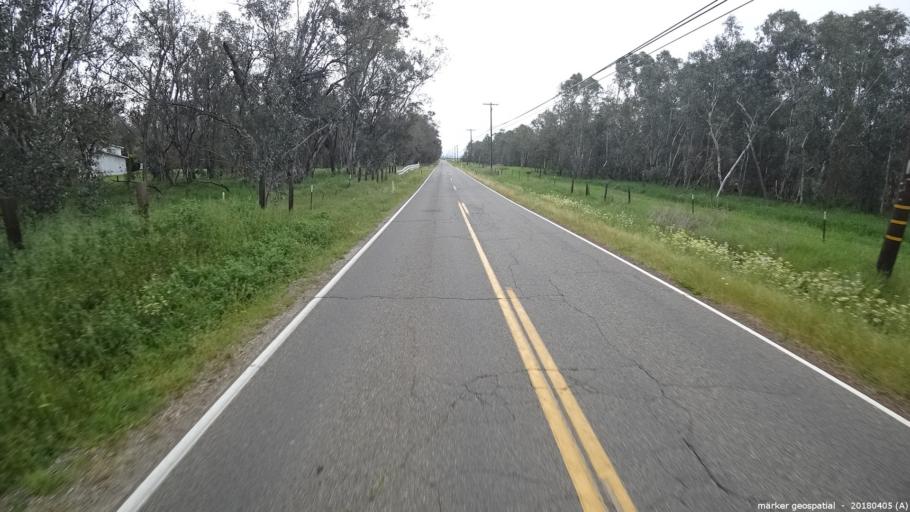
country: US
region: California
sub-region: Sacramento County
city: Clay
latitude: 38.2926
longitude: -121.1791
